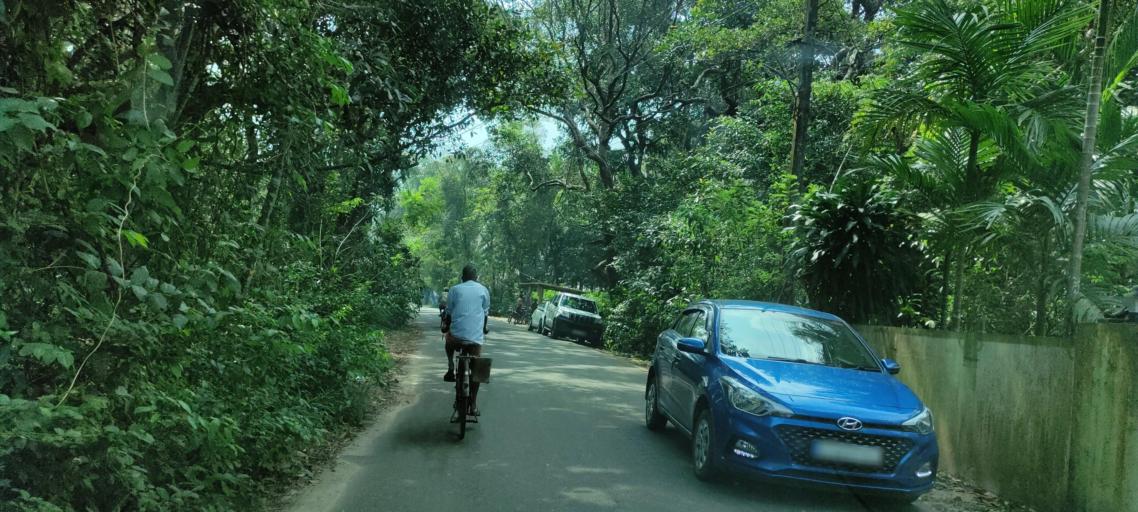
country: IN
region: Kerala
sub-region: Alappuzha
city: Shertallai
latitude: 9.6266
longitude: 76.3506
